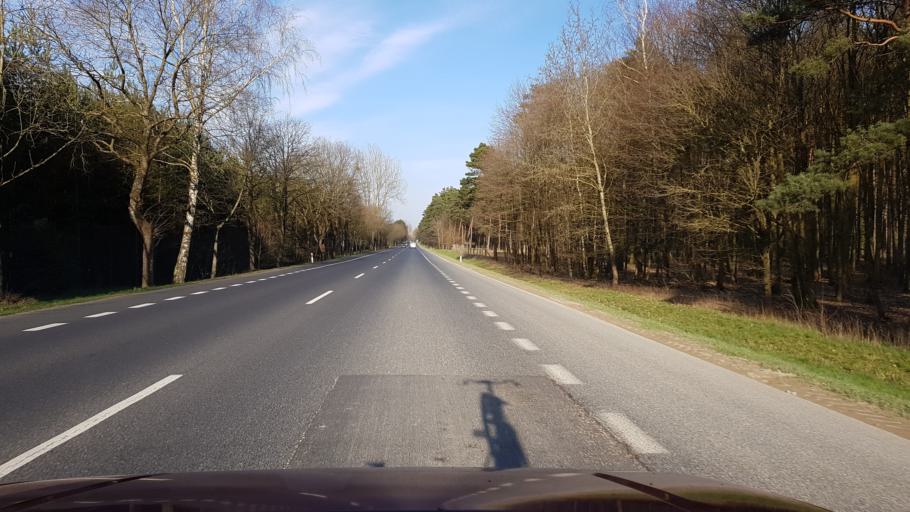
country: PL
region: West Pomeranian Voivodeship
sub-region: Powiat kolobrzeski
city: Goscino
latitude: 53.9686
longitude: 15.6560
